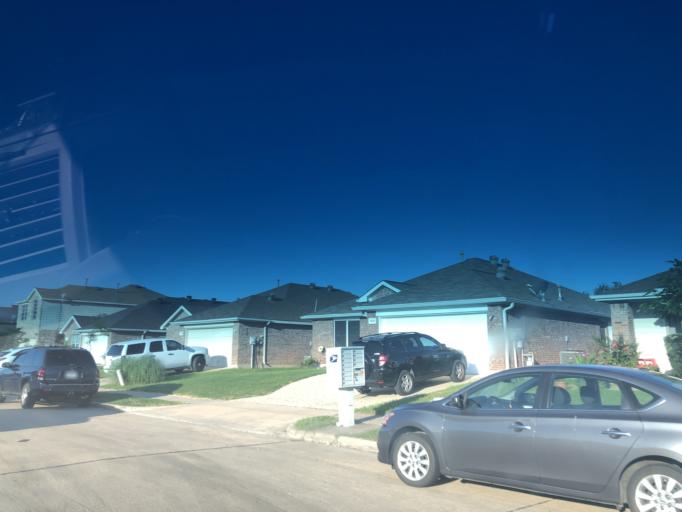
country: US
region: Texas
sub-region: Dallas County
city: Grand Prairie
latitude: 32.7003
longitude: -97.0198
